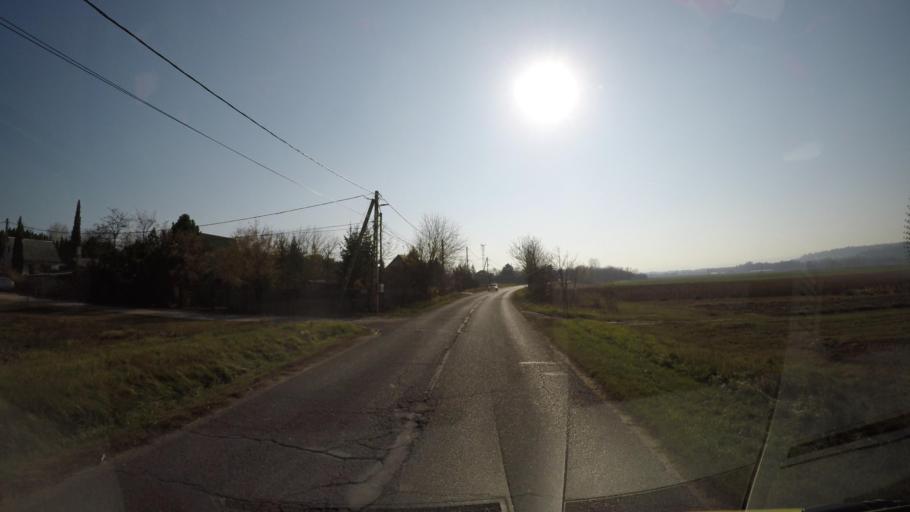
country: HU
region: Pest
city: Leanyfalu
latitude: 47.7052
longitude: 19.1073
